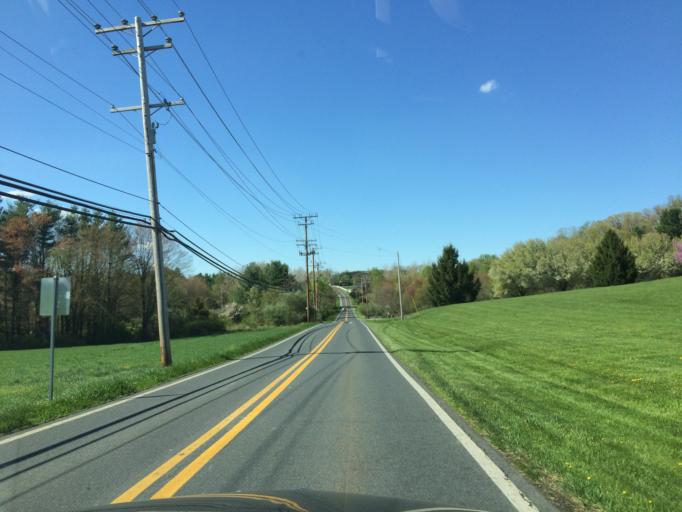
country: US
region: Maryland
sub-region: Carroll County
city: Sykesville
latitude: 39.4070
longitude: -76.9955
